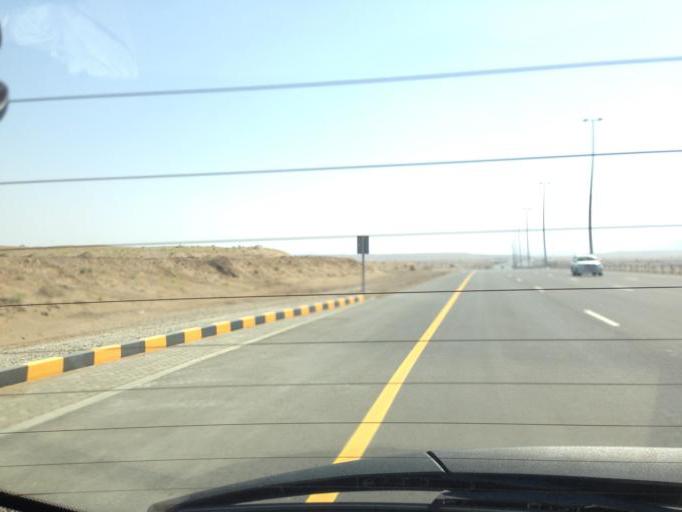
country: OM
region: Al Batinah
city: Rustaq
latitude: 23.5297
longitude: 57.5925
